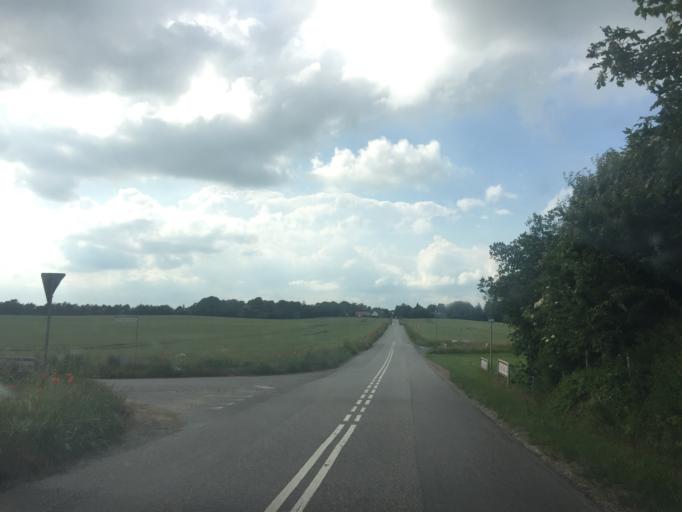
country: DK
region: Capital Region
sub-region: Hoje-Taastrup Kommune
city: Flong
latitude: 55.6888
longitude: 12.1745
